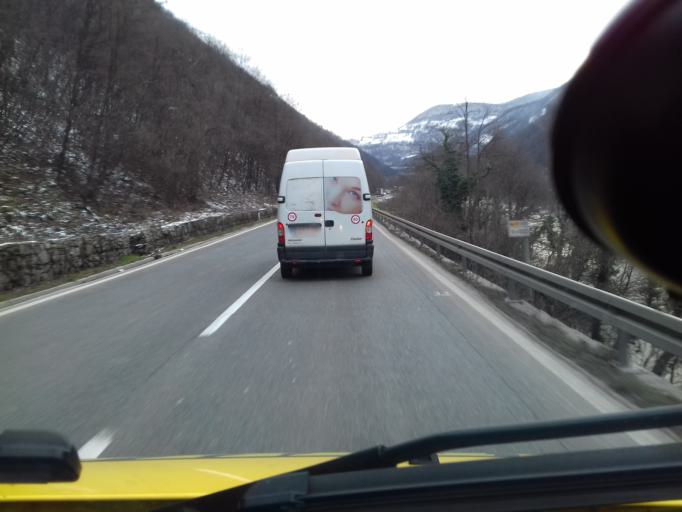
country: BA
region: Federation of Bosnia and Herzegovina
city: Lokvine
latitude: 44.2765
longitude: 17.8821
